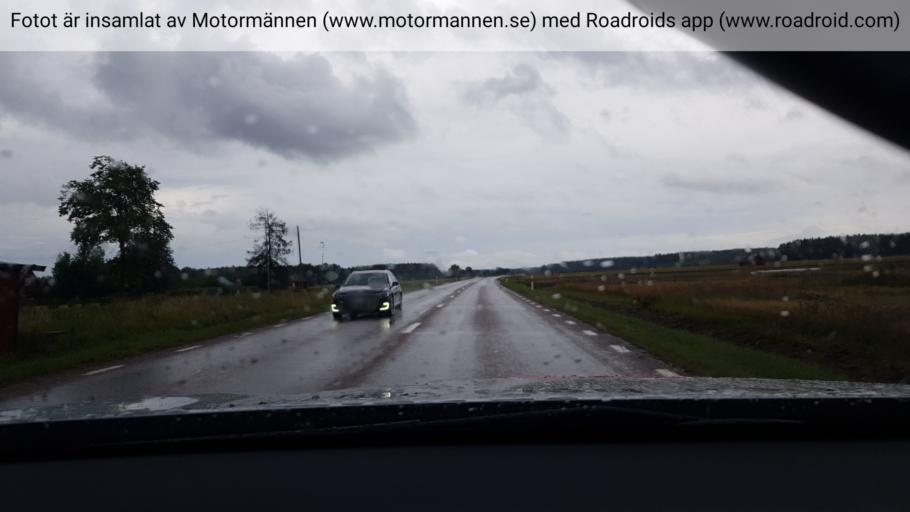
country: SE
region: Uppsala
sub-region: Tierps Kommun
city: Karlholmsbruk
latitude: 60.4635
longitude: 17.7659
